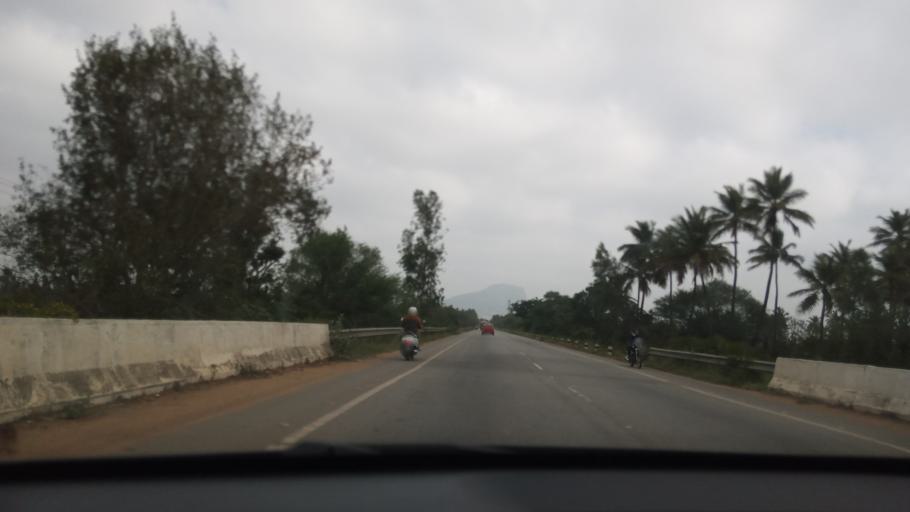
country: IN
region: Karnataka
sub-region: Chikkaballapur
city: Chintamani
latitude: 13.3074
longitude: 77.9751
